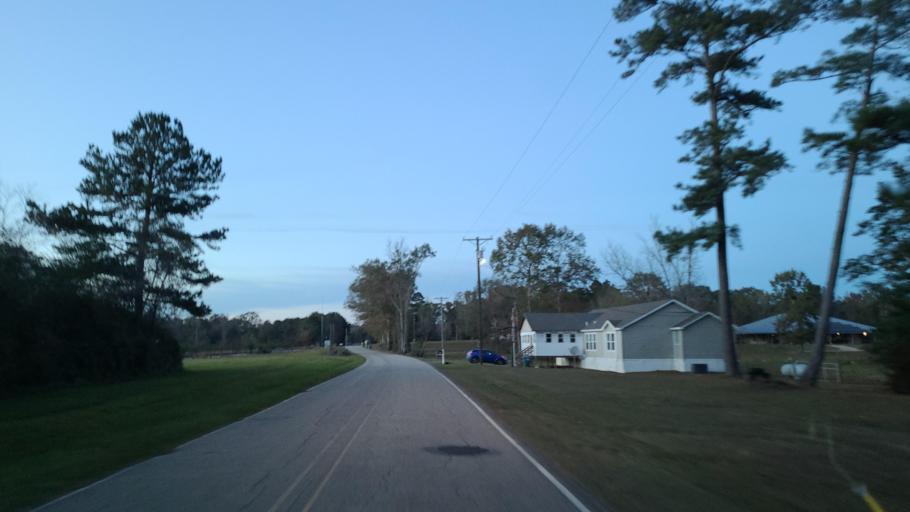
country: US
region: Mississippi
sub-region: Perry County
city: New Augusta
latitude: 31.1599
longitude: -89.2119
